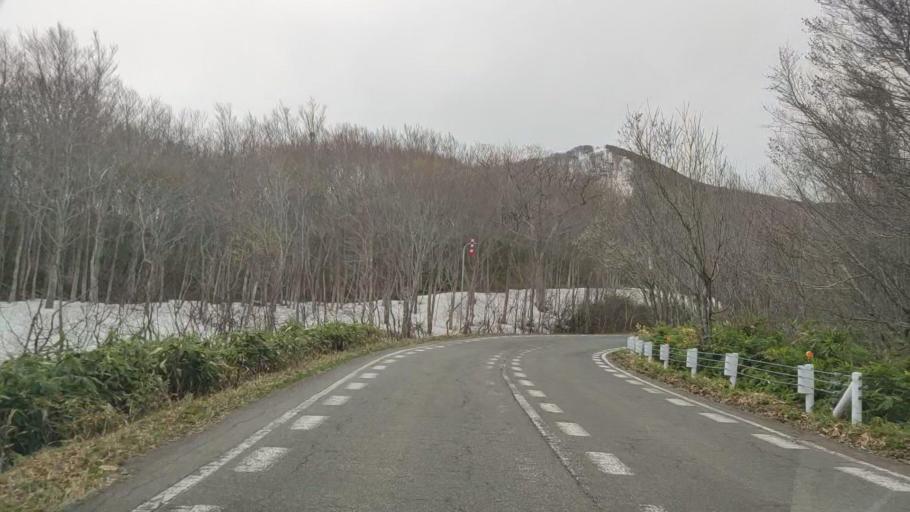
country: JP
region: Aomori
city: Aomori Shi
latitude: 40.6570
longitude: 140.9555
